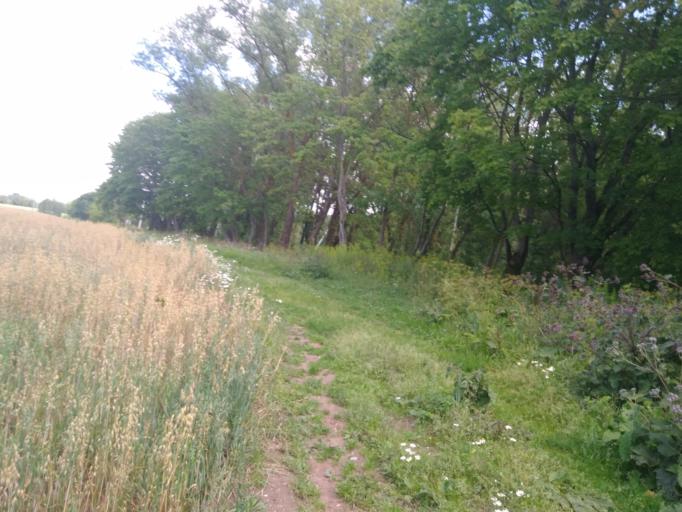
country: BY
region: Minsk
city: Minsk
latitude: 53.9432
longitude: 27.5563
